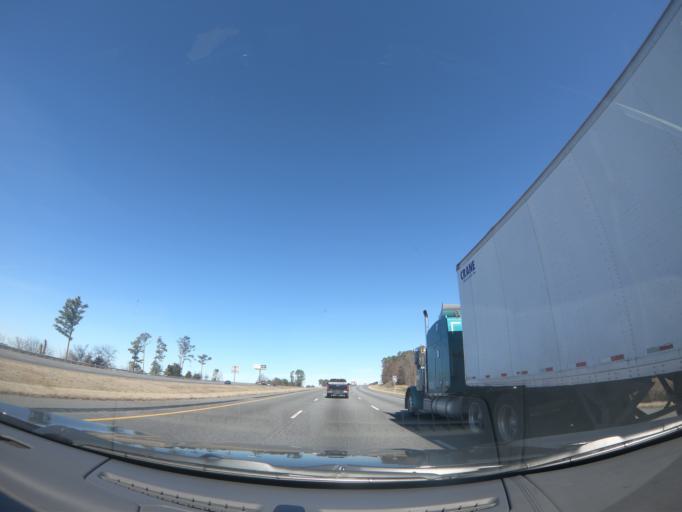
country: US
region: Georgia
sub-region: Bartow County
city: Adairsville
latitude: 34.3836
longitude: -84.9163
